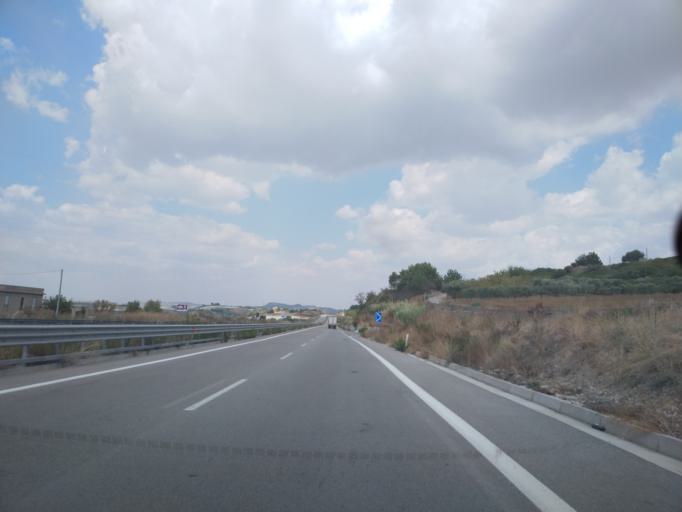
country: IT
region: Sicily
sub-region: Agrigento
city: Canicatti
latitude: 37.3849
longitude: 13.8277
